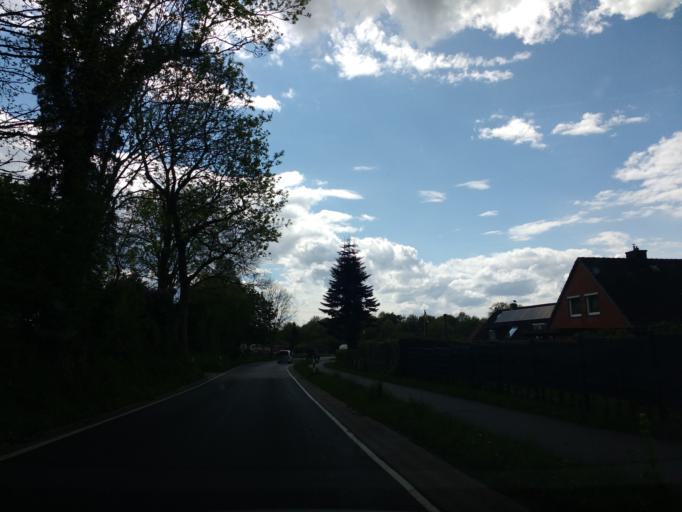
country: DE
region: Schleswig-Holstein
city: Eckernforde
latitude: 54.4876
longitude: 9.8610
